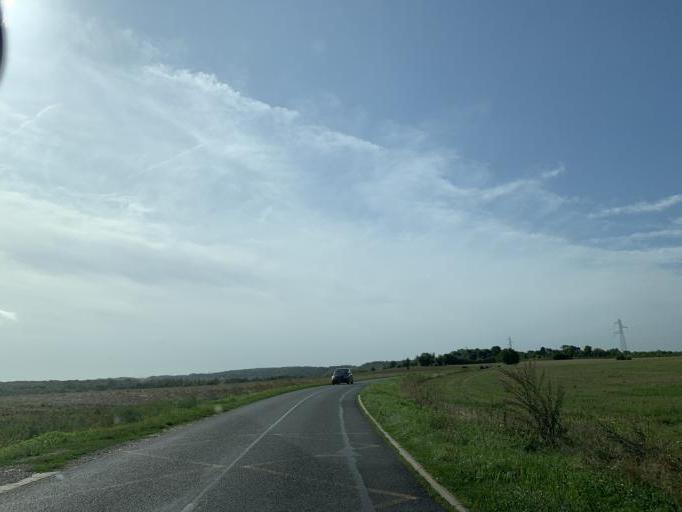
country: FR
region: Ile-de-France
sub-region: Departement de Seine-et-Marne
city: Chalifert
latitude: 48.9130
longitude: 2.7674
